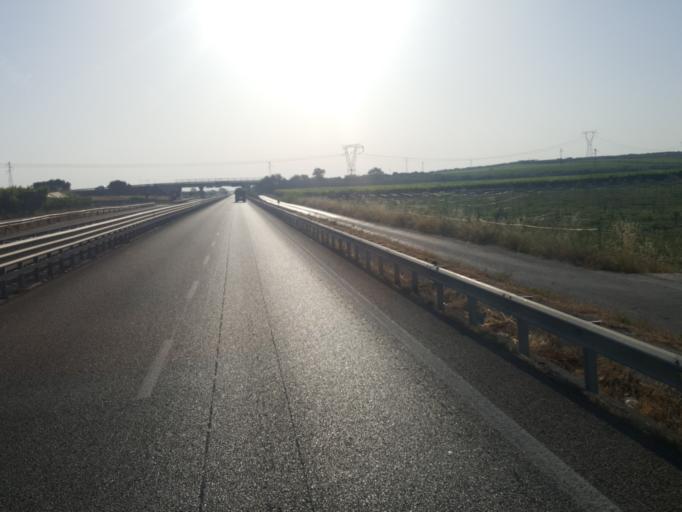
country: IT
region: Apulia
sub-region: Provincia di Barletta - Andria - Trani
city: San Ferdinando di Puglia
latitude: 41.2821
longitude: 15.9964
